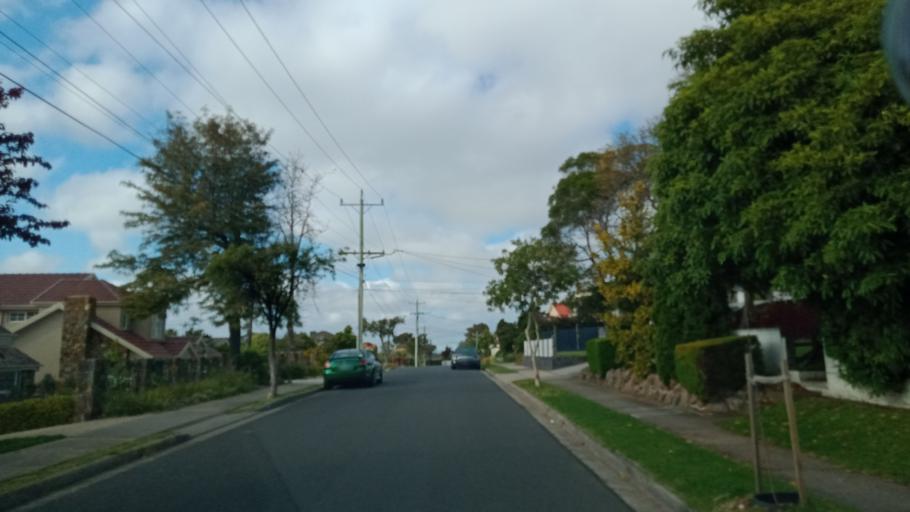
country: AU
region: Victoria
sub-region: Monash
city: Notting Hill
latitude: -37.8900
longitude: 145.1527
